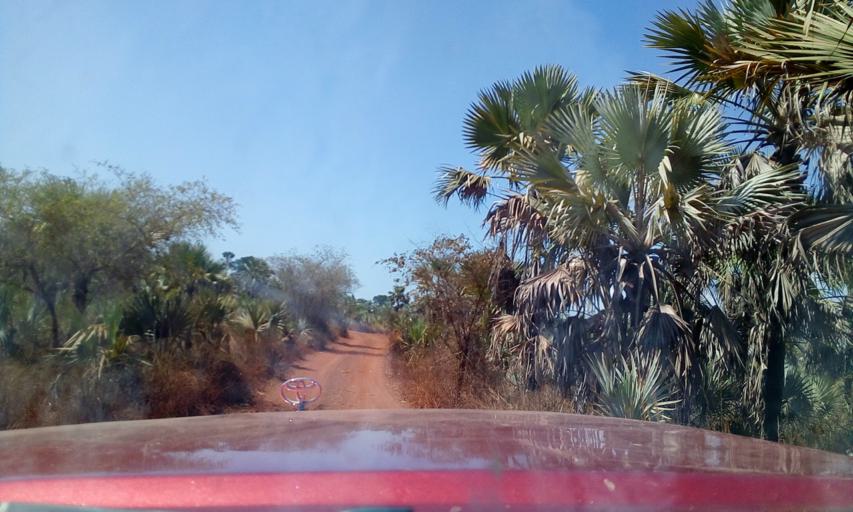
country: MG
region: Boeny
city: Sitampiky
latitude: -16.1253
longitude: 45.4345
